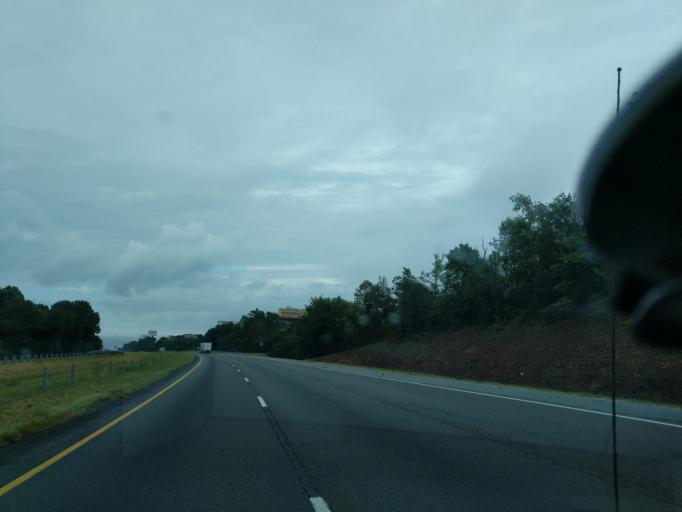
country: US
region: Georgia
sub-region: Jackson County
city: Commerce
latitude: 34.2301
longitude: -83.4985
